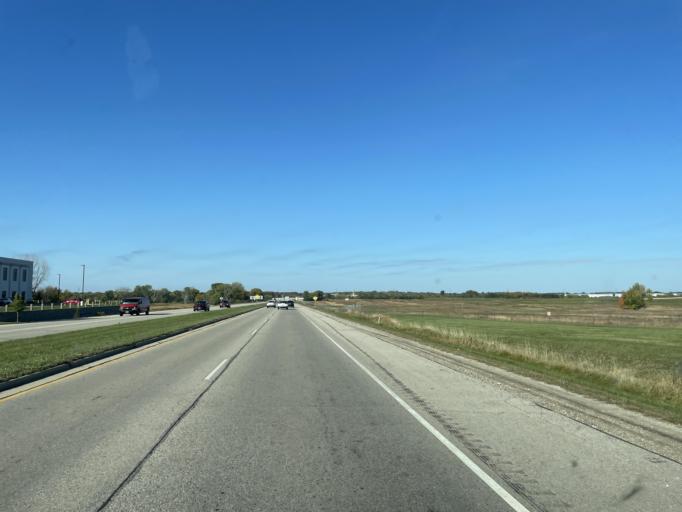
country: US
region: Wisconsin
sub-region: Kenosha County
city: Pleasant Prairie
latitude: 42.5896
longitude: -87.9361
